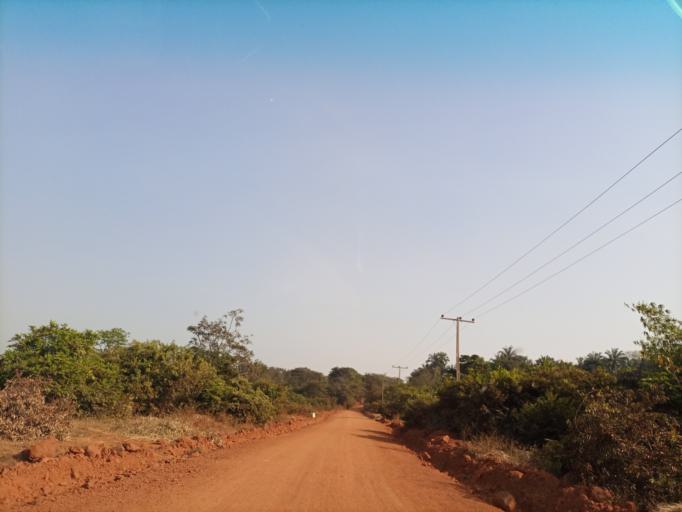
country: NG
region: Enugu
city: Opi
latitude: 6.7667
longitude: 7.3942
